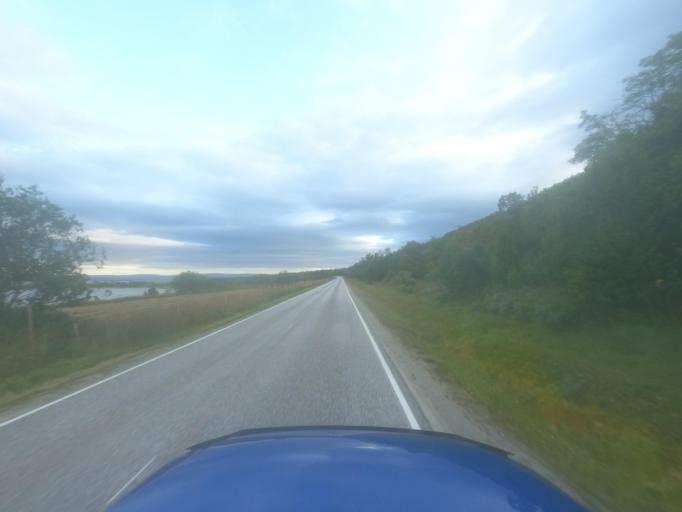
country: NO
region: Finnmark Fylke
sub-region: Porsanger
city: Lakselv
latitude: 70.4736
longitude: 25.2226
